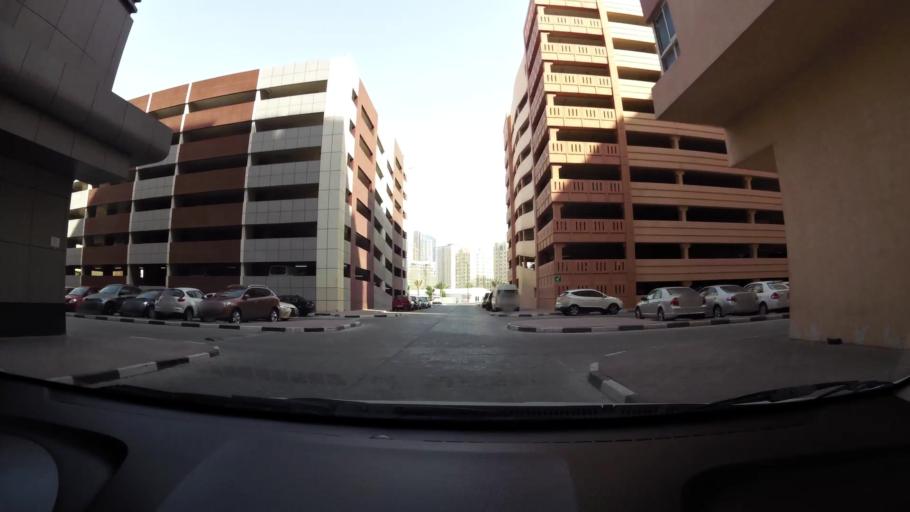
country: AE
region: Ash Shariqah
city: Sharjah
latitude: 25.2917
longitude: 55.3680
